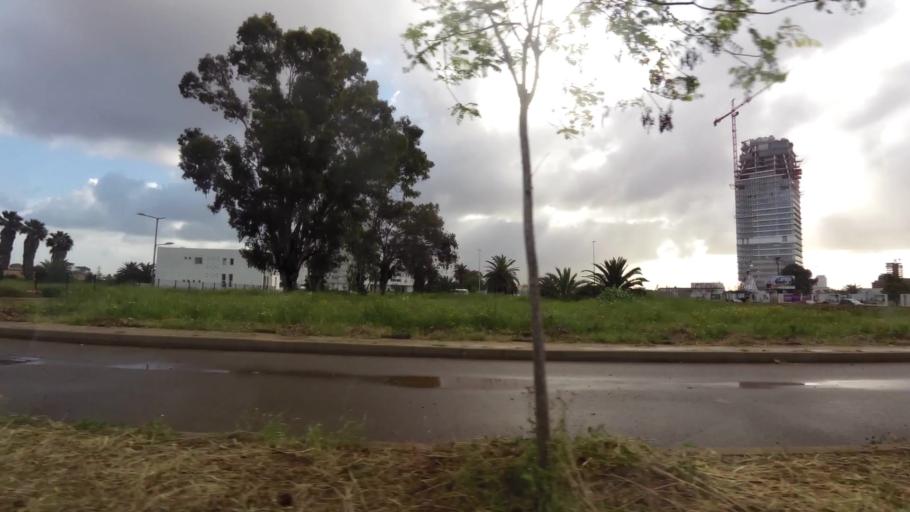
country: MA
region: Grand Casablanca
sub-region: Casablanca
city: Casablanca
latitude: 33.5641
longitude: -7.6648
